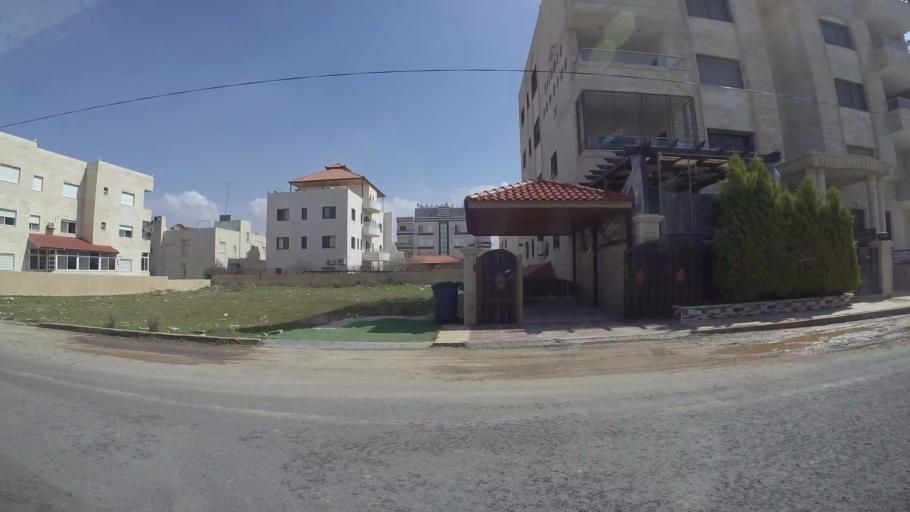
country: JO
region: Amman
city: Al Bunayyat ash Shamaliyah
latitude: 31.9007
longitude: 35.8883
